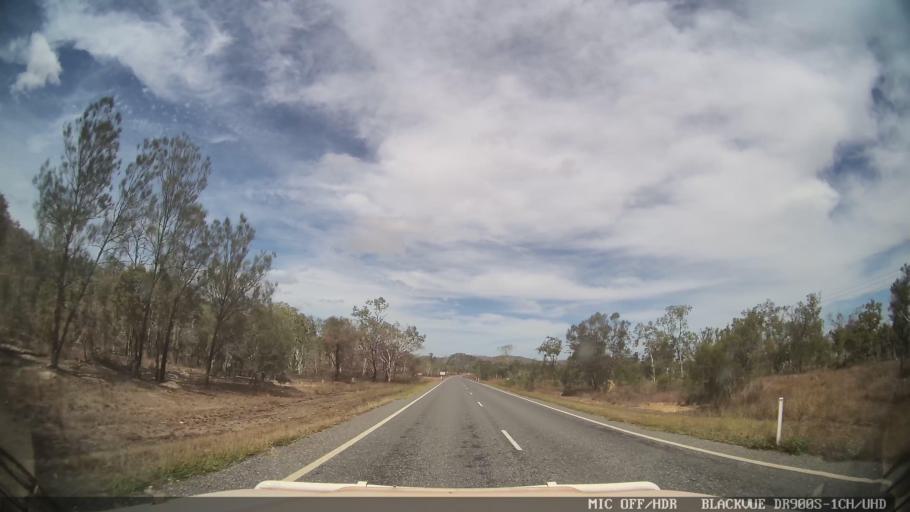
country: AU
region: Queensland
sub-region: Tablelands
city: Mareeba
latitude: -16.7831
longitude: 145.3466
